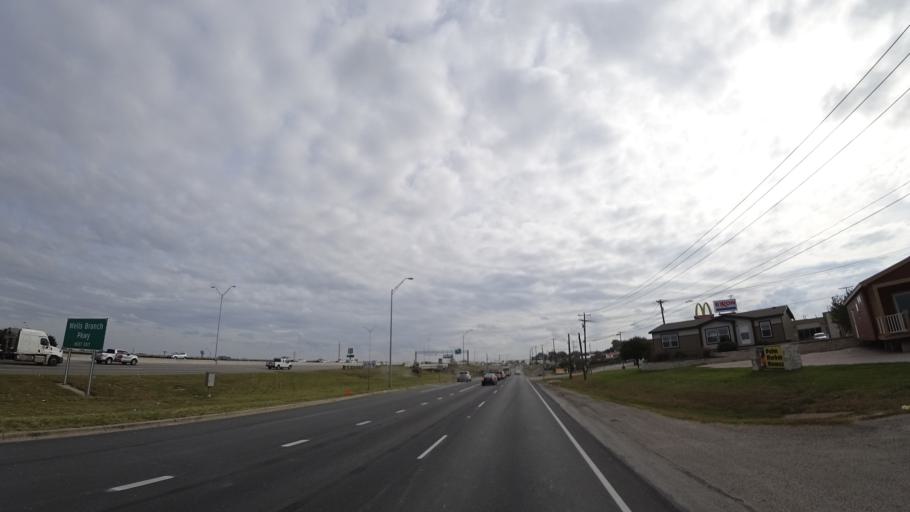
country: US
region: Texas
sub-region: Travis County
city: Wells Branch
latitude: 30.4576
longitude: -97.6673
